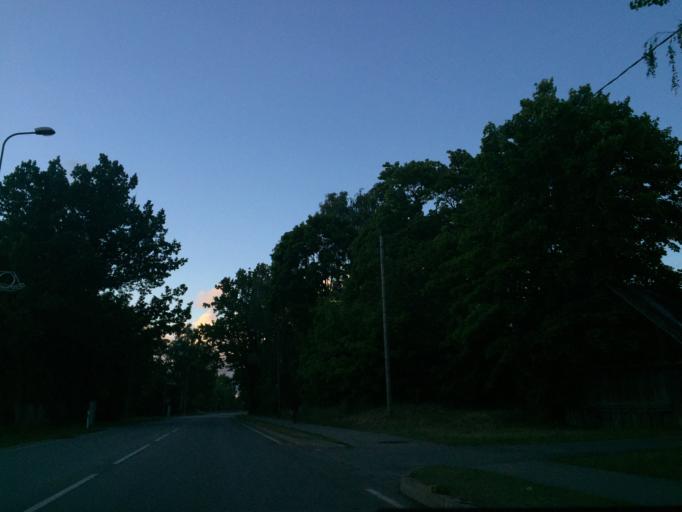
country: LV
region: Saulkrastu
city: Saulkrasti
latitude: 57.3088
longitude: 24.4114
